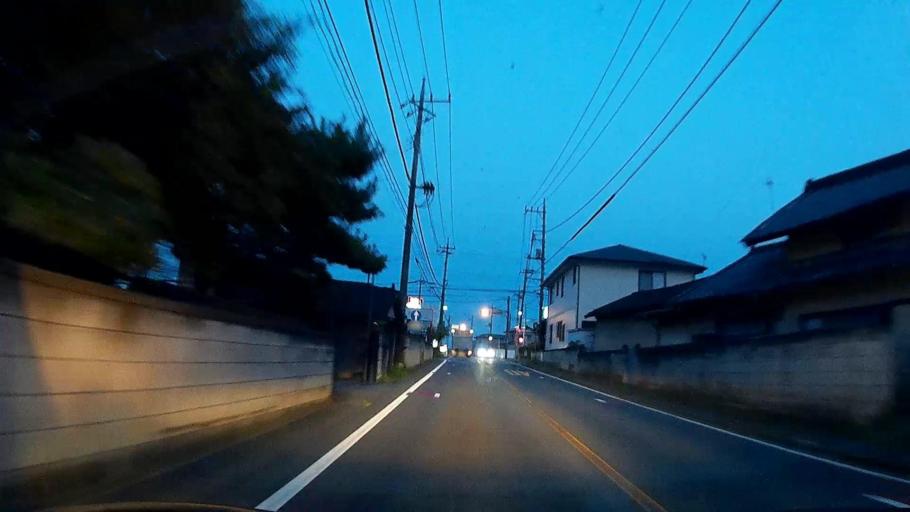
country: JP
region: Gunma
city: Takasaki
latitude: 36.3437
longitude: 138.9648
